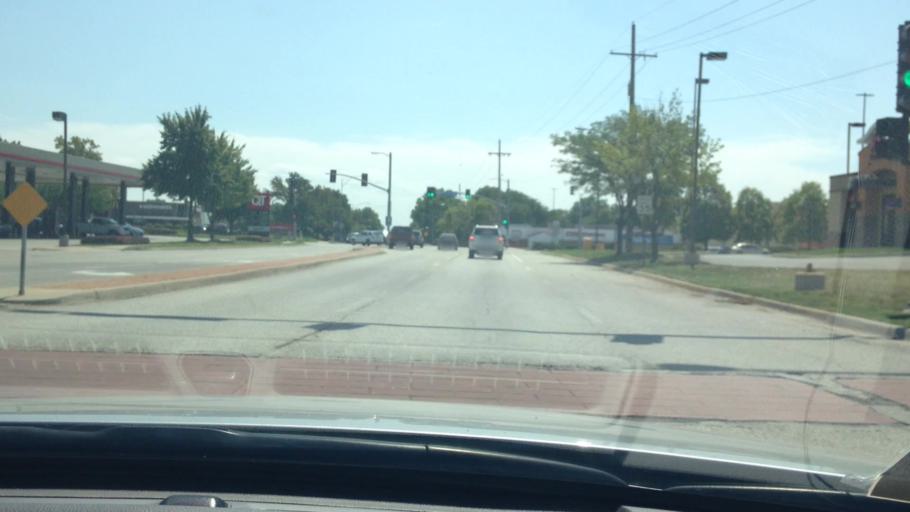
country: US
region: Kansas
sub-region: Johnson County
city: Roeland Park
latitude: 39.0376
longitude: -94.6398
